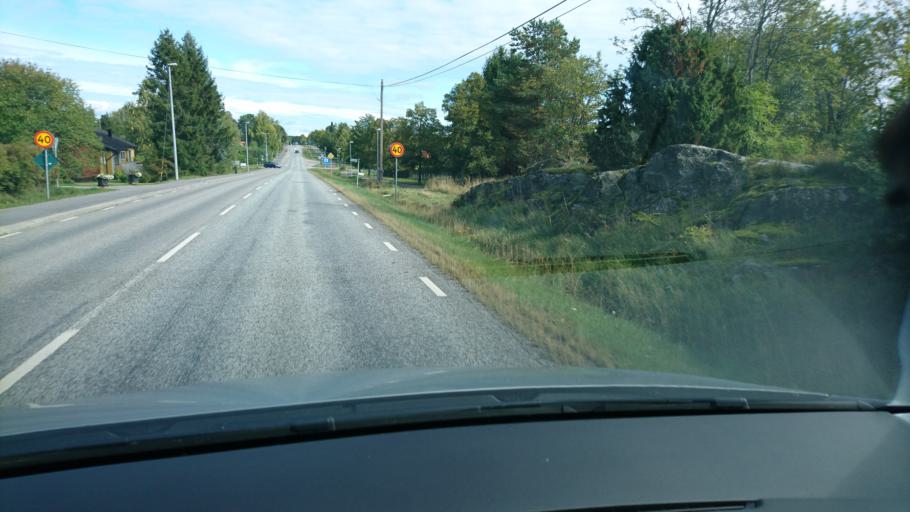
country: SE
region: Soedermanland
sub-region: Strangnas Kommun
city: Stallarholmen
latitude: 59.3536
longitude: 17.1973
